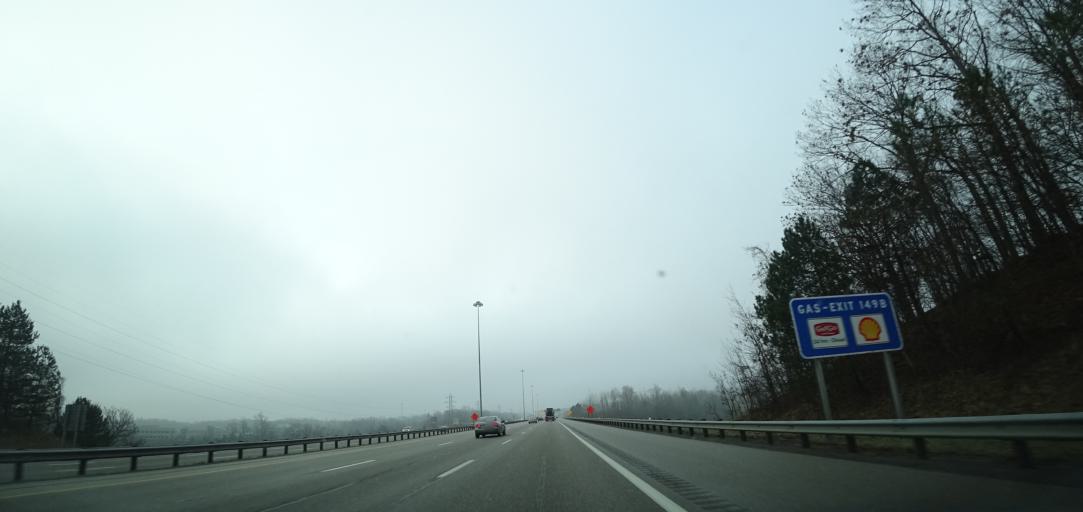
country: US
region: Ohio
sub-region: Cuyahoga County
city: Brecksville
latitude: 41.3223
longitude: -81.6491
